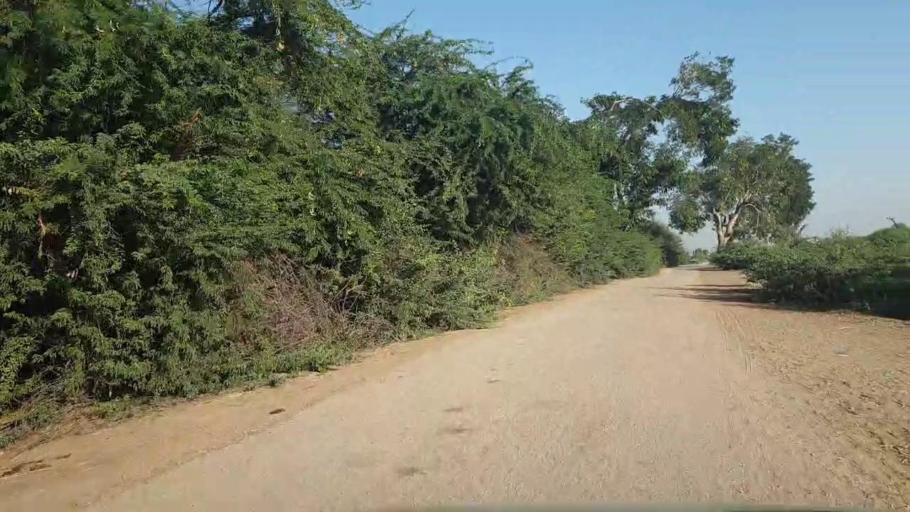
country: PK
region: Sindh
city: Badin
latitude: 24.6892
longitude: 68.8160
